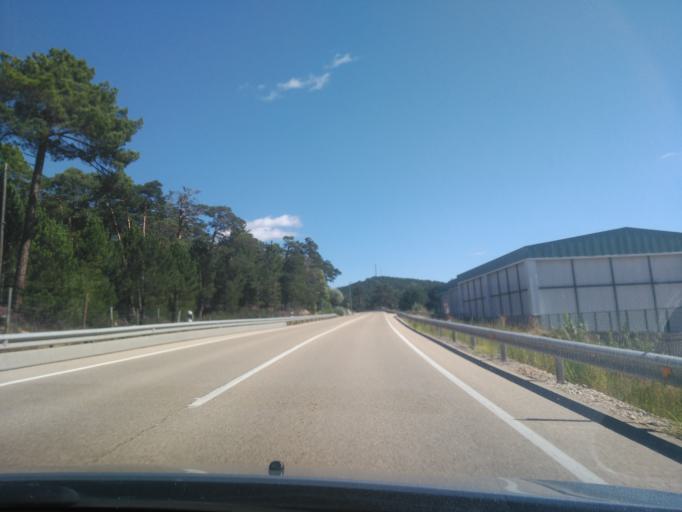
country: ES
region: Castille and Leon
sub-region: Provincia de Soria
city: Navaleno
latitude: 41.8391
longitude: -3.0173
